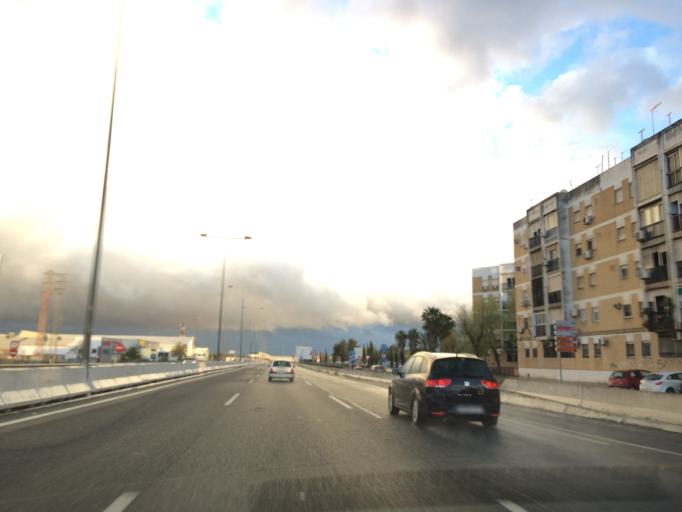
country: ES
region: Andalusia
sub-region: Provincia de Sevilla
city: Alcala de Guadaira
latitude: 37.3510
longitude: -5.8416
